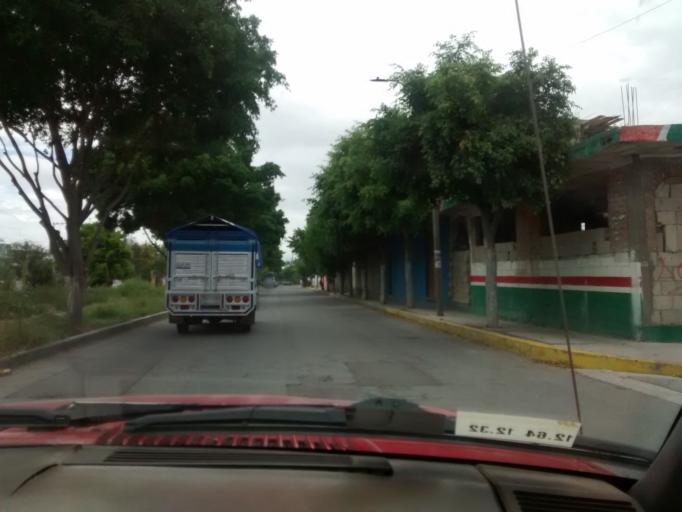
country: MX
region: Puebla
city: Tehuacan
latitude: 18.4708
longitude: -97.4055
